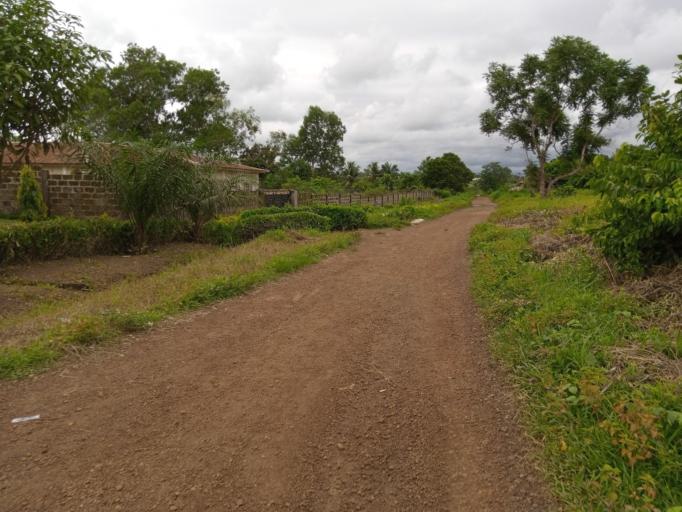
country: SL
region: Southern Province
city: Moyamba
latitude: 8.1678
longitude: -12.4262
